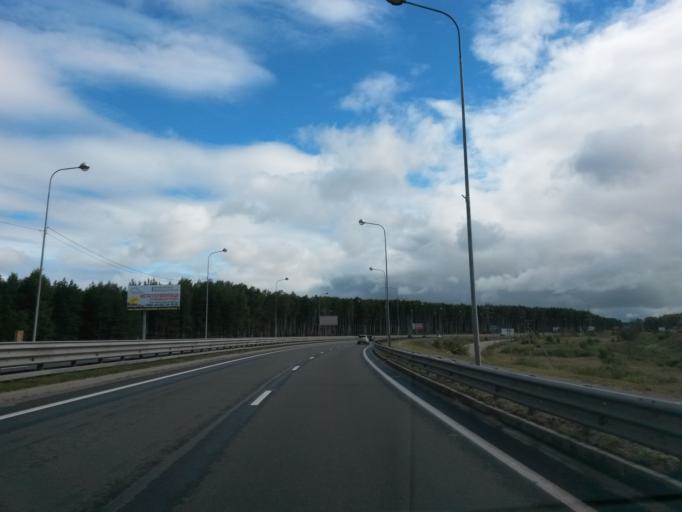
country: RU
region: Jaroslavl
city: Yaroslavl
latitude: 57.6829
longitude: 39.8749
